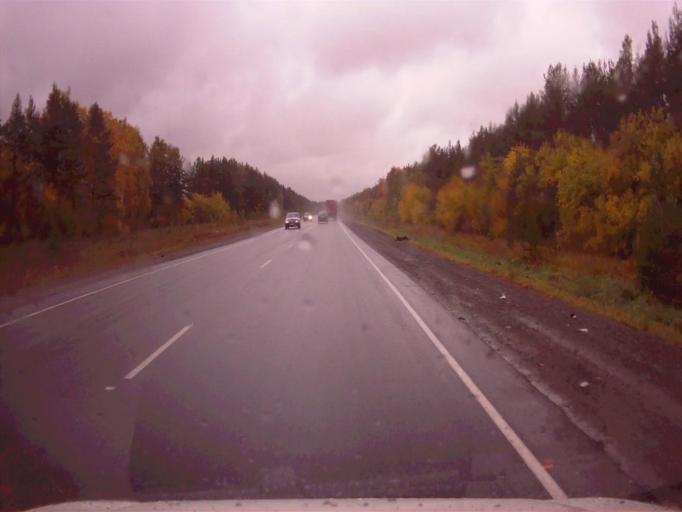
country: RU
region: Chelyabinsk
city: Roshchino
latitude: 55.3563
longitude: 61.2551
